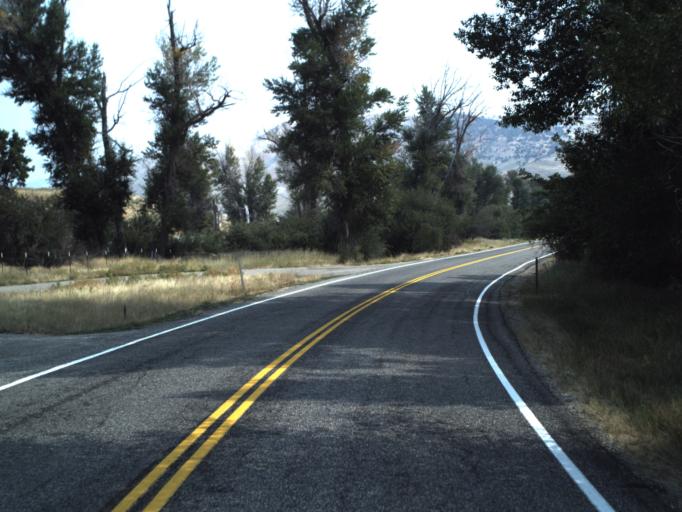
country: US
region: Utah
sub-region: Morgan County
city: Morgan
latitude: 40.9855
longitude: -111.5364
